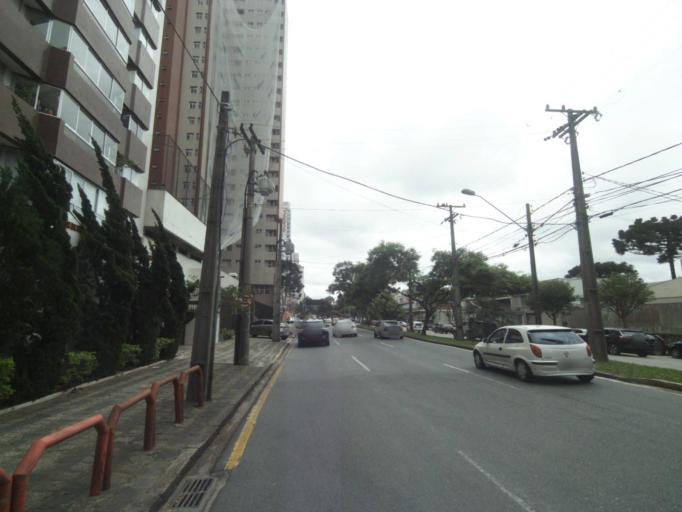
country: BR
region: Parana
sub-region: Curitiba
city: Curitiba
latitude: -25.4469
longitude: -49.2868
